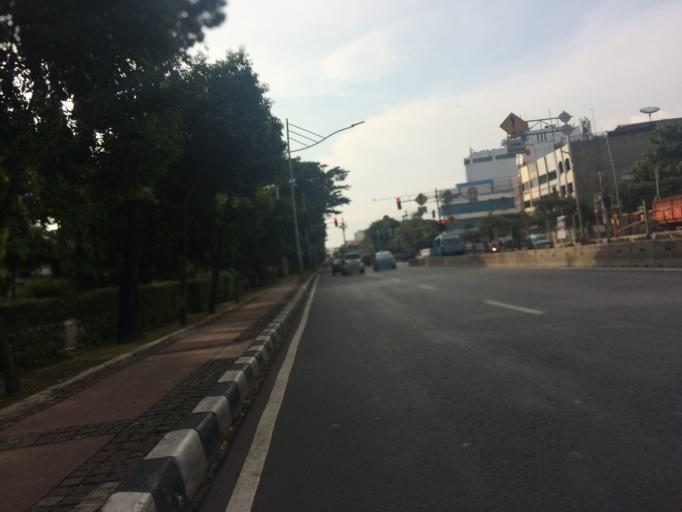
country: ID
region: Jakarta Raya
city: Jakarta
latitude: -6.1690
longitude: 106.8397
